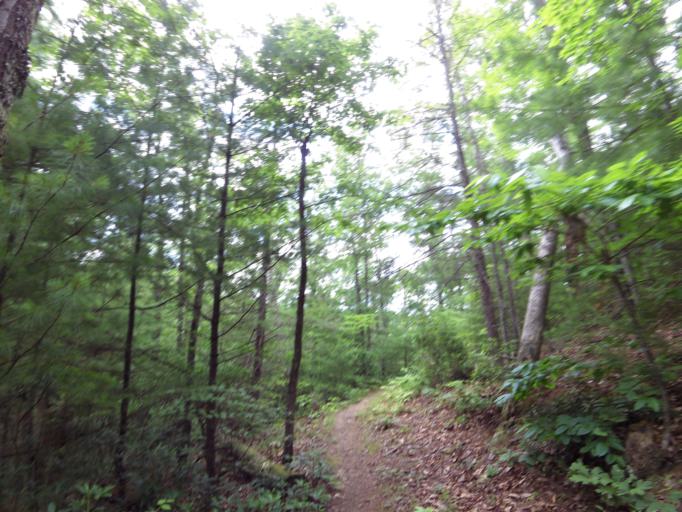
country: US
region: Tennessee
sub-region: Blount County
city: Wildwood
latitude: 35.6664
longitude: -83.8314
